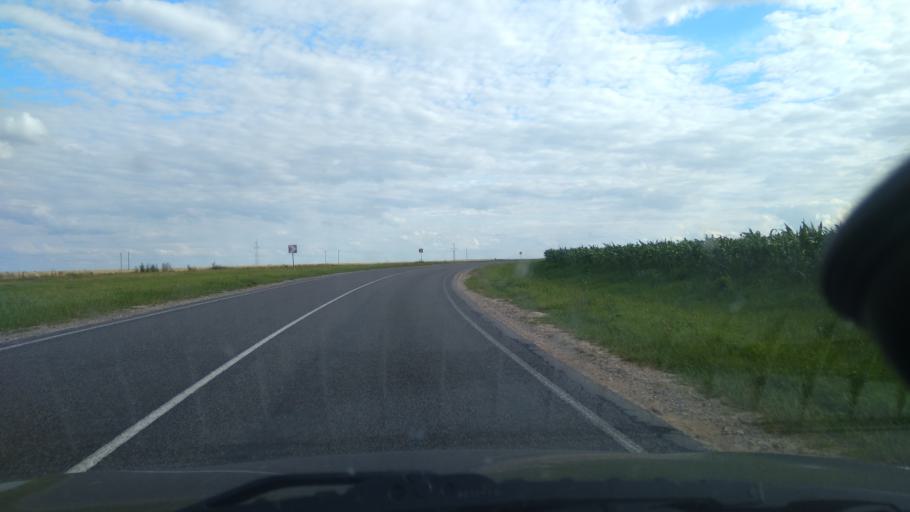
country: BY
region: Grodnenskaya
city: Masty
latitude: 53.3110
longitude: 24.6963
